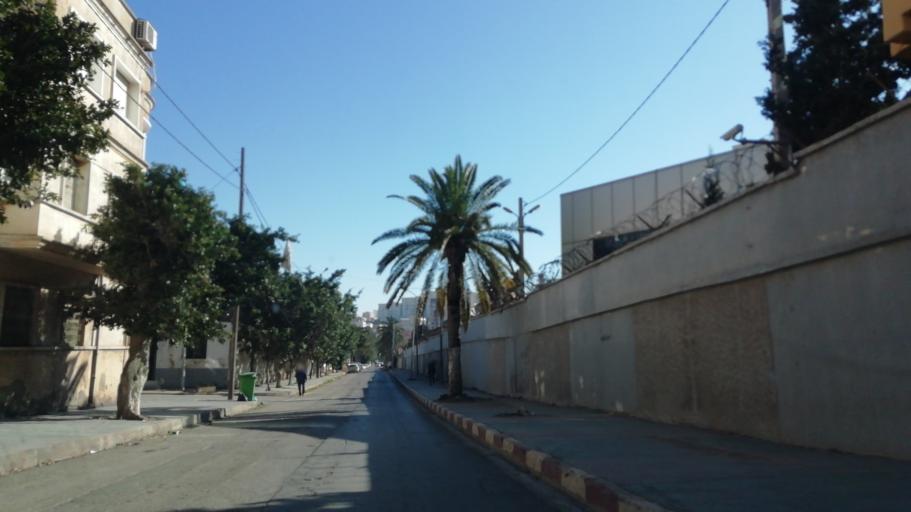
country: DZ
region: Oran
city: Oran
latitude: 35.7116
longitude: -0.6231
